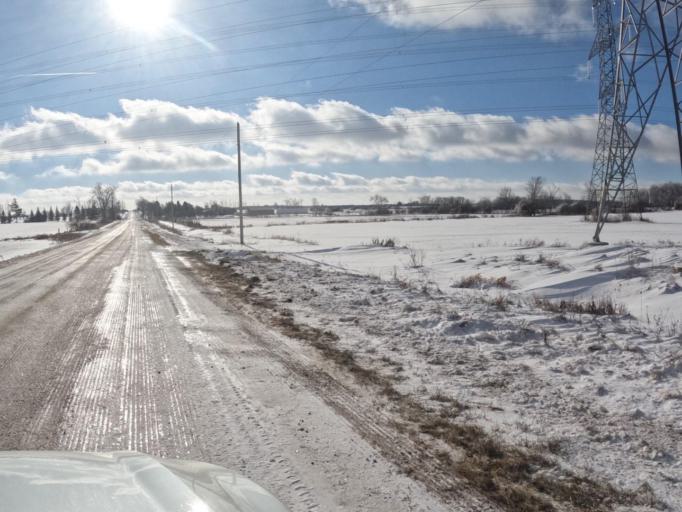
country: CA
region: Ontario
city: Shelburne
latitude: 43.9951
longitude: -80.4083
